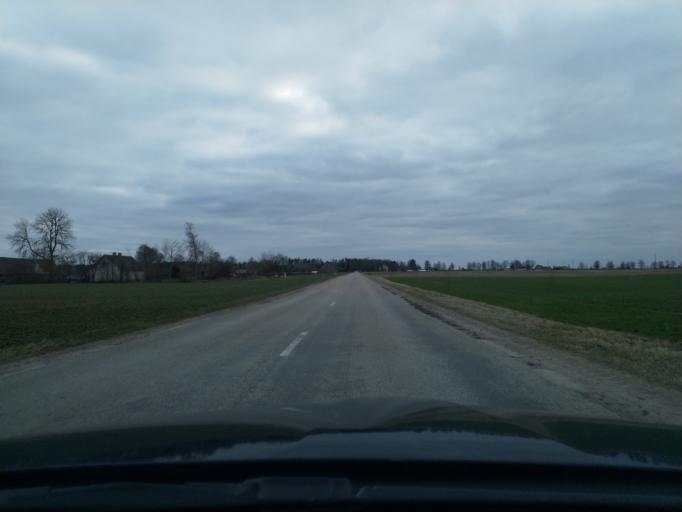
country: LV
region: Talsu Rajons
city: Sabile
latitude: 56.9420
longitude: 22.5974
